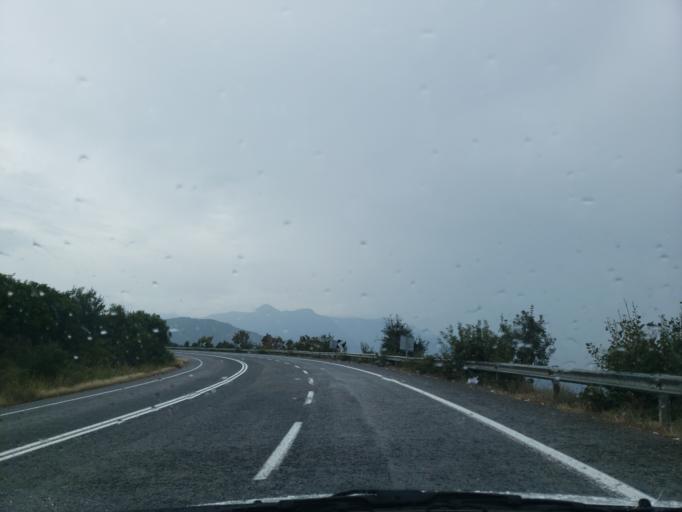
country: GR
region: Central Greece
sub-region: Nomos Fthiotidos
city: Anthili
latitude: 38.7944
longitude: 22.4767
